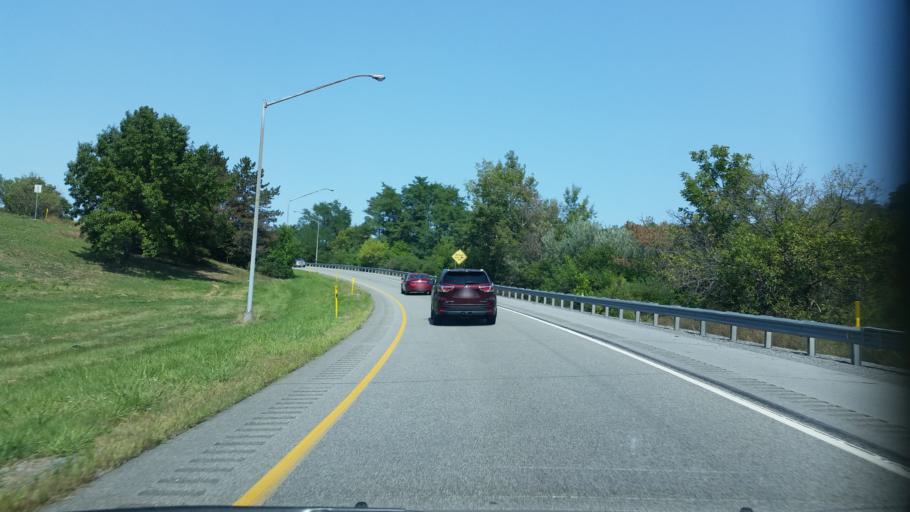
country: US
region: Pennsylvania
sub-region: Blair County
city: Duncansville
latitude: 40.4386
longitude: -78.4244
